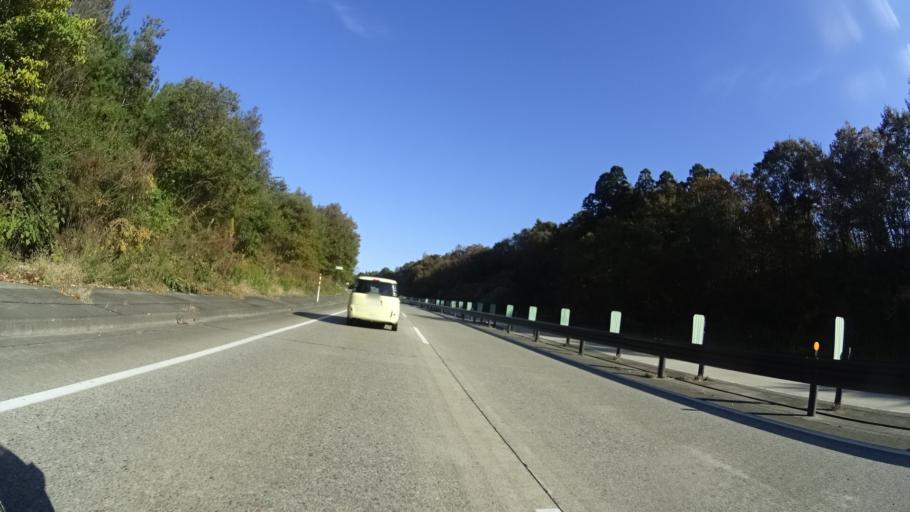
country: JP
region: Ishikawa
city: Komatsu
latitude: 36.3485
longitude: 136.4511
